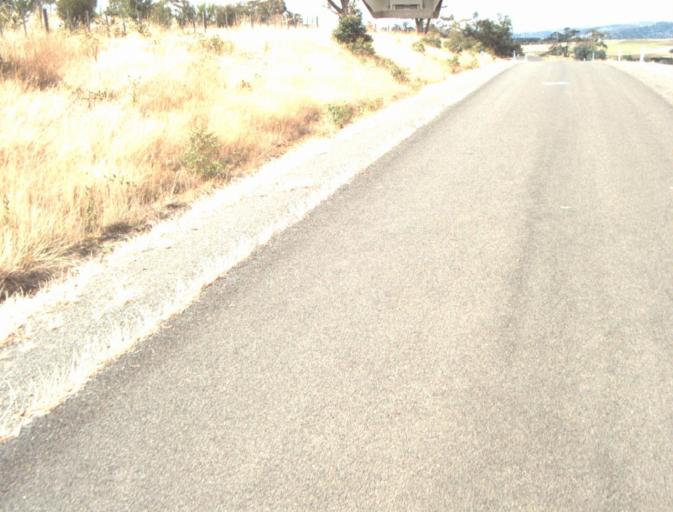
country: AU
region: Tasmania
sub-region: Launceston
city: Mayfield
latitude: -41.3447
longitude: 147.0867
